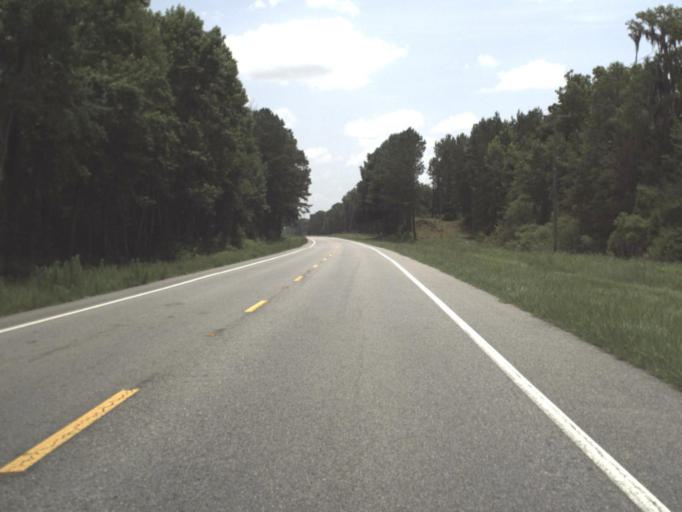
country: US
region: Florida
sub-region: Madison County
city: Madison
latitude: 30.4816
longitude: -83.5390
